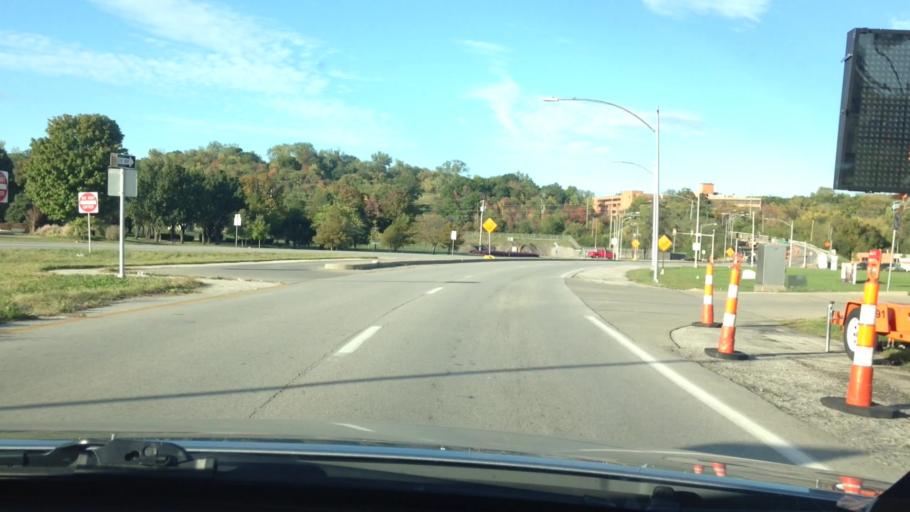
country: US
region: Missouri
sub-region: Clay County
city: North Kansas City
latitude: 39.1507
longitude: -94.5800
